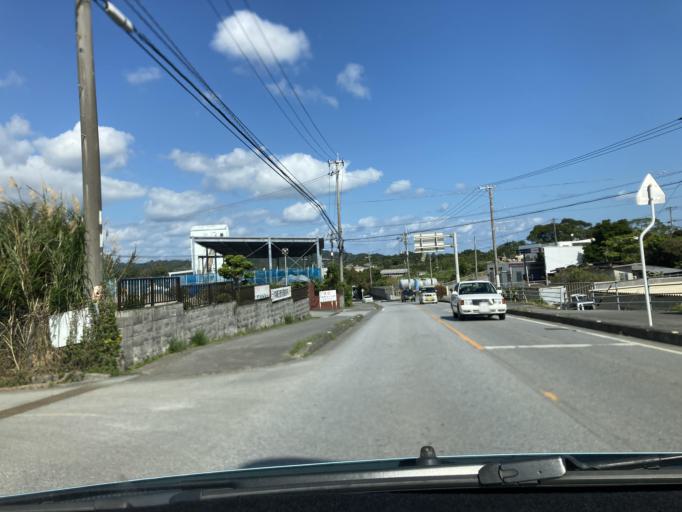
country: JP
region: Okinawa
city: Nago
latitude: 26.6133
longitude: 128.0006
